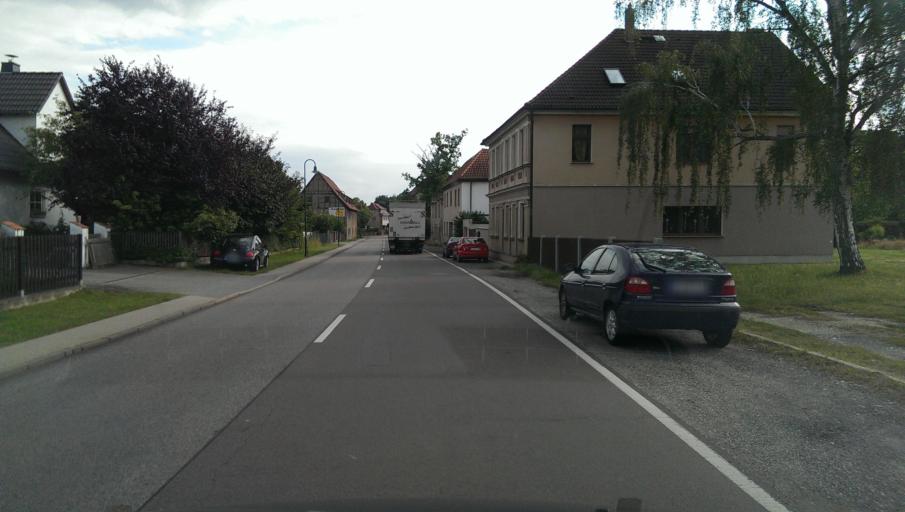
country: DE
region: Saxony
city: Elstertrebnitz
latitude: 51.1170
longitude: 12.1990
